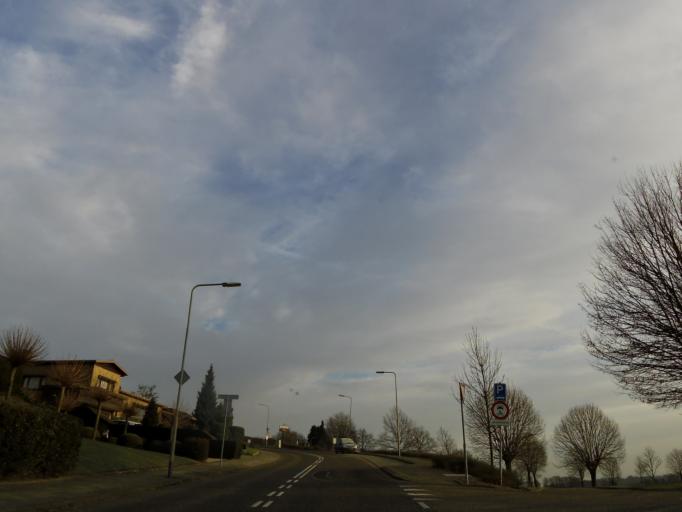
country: NL
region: Limburg
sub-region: Gemeente Simpelveld
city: Simpelveld
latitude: 50.8402
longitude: 5.9758
